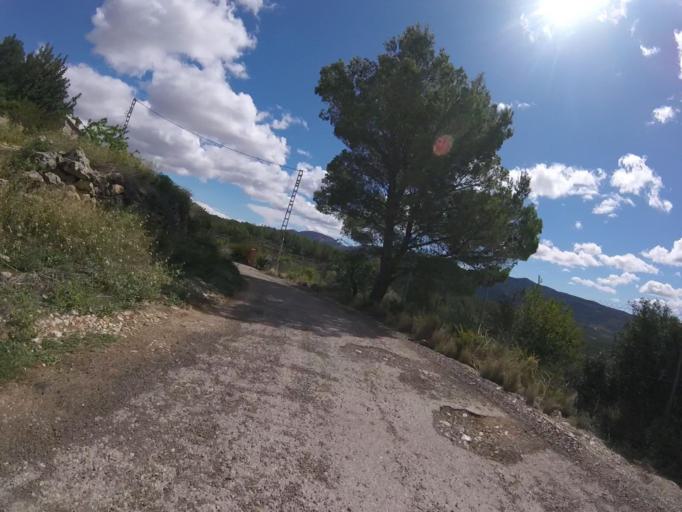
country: ES
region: Valencia
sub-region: Provincia de Castello
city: Sierra-Engarceran
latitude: 40.2687
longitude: -0.1005
